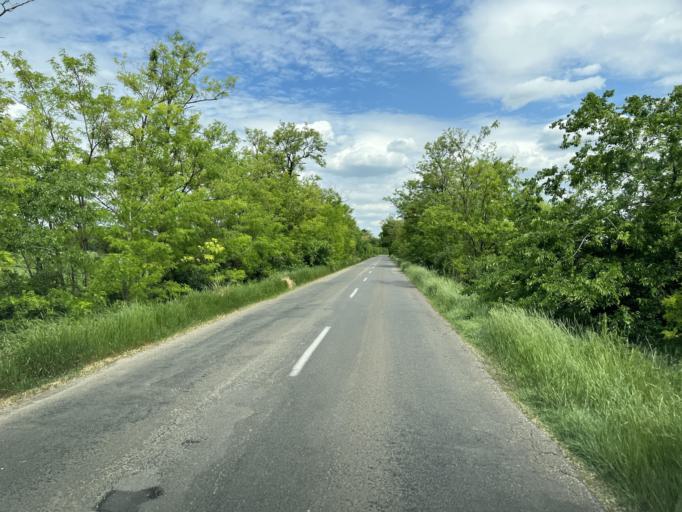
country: HU
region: Pest
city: Forropuszta
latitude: 47.4818
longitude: 19.6357
